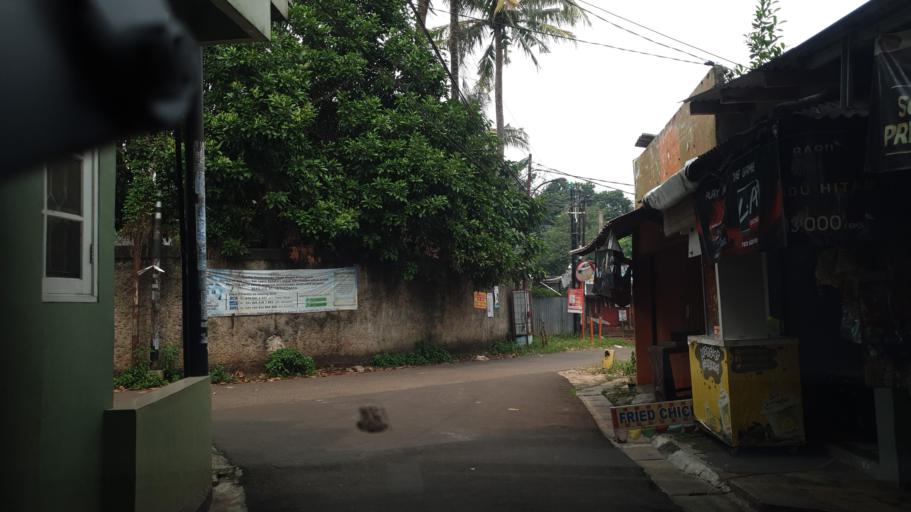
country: ID
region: West Java
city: Pamulang
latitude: -6.3315
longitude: 106.7737
